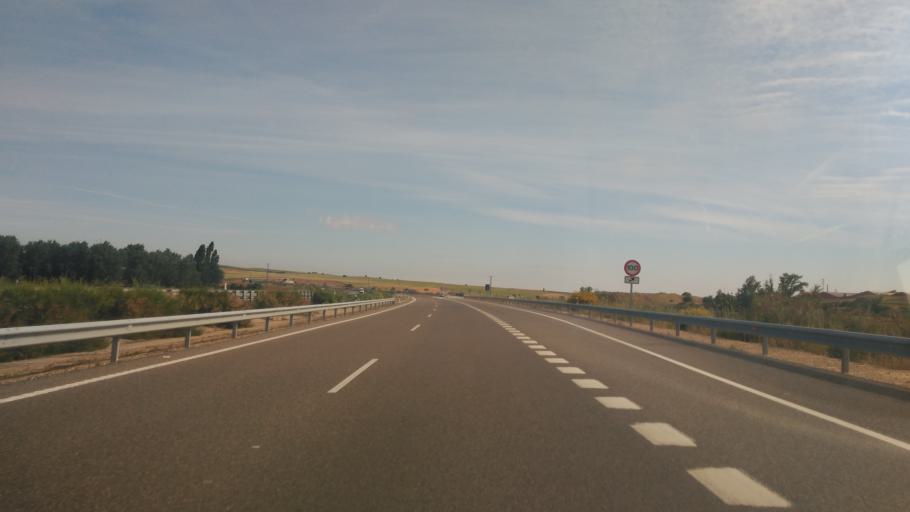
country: ES
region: Castille and Leon
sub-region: Provincia de Zamora
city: Corrales
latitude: 41.3551
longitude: -5.7131
